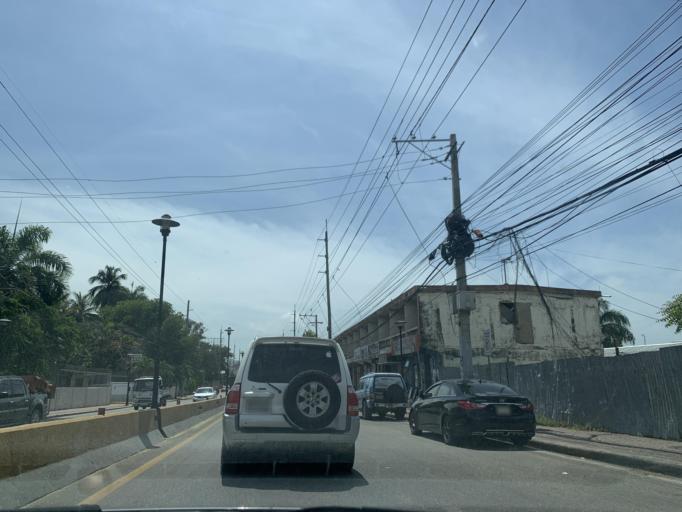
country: DO
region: Puerto Plata
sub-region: Puerto Plata
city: Puerto Plata
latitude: 19.7921
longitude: -70.7056
